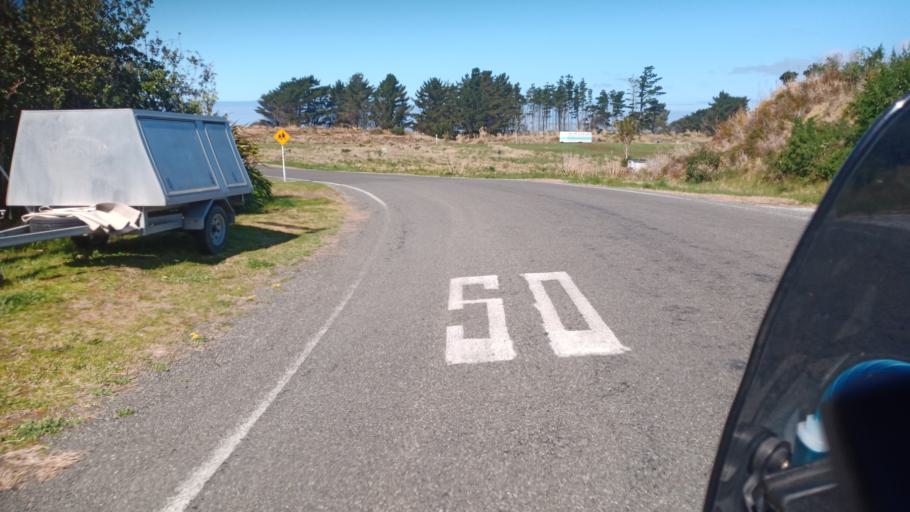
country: NZ
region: Gisborne
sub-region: Gisborne District
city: Gisborne
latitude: -39.0177
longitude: 177.8825
